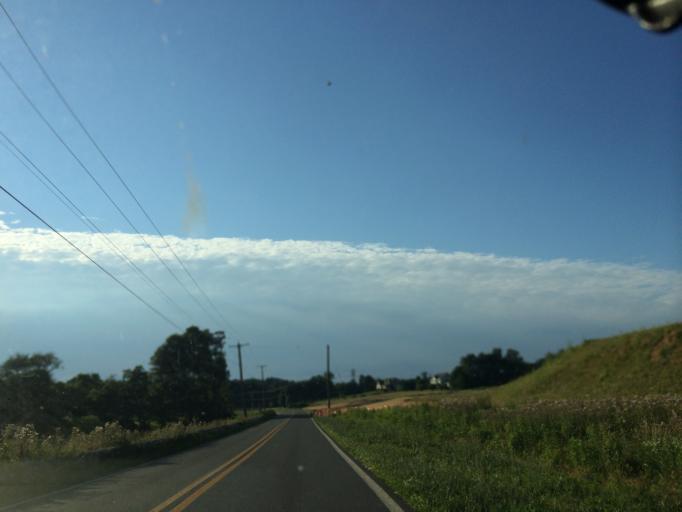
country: US
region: Maryland
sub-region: Carroll County
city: Eldersburg
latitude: 39.4394
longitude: -76.9768
